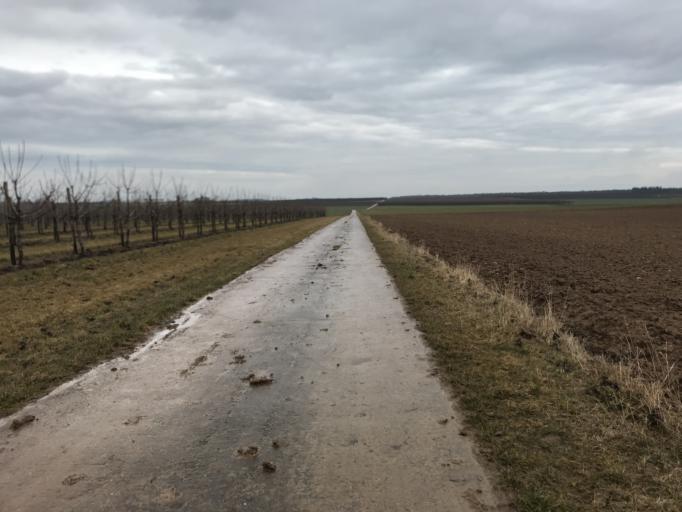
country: DE
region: Rheinland-Pfalz
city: Essenheim
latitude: 49.9410
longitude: 8.1576
